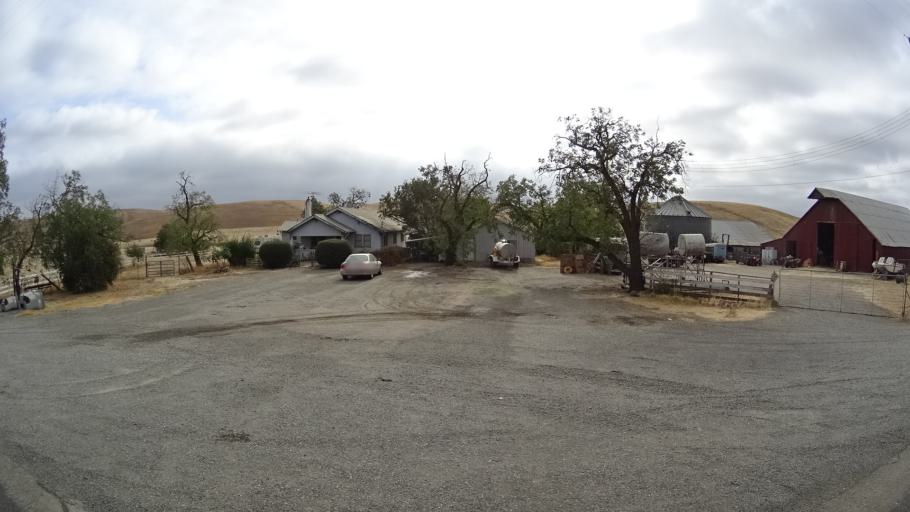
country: US
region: California
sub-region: Yolo County
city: Dunnigan
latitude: 38.7890
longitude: -121.9175
